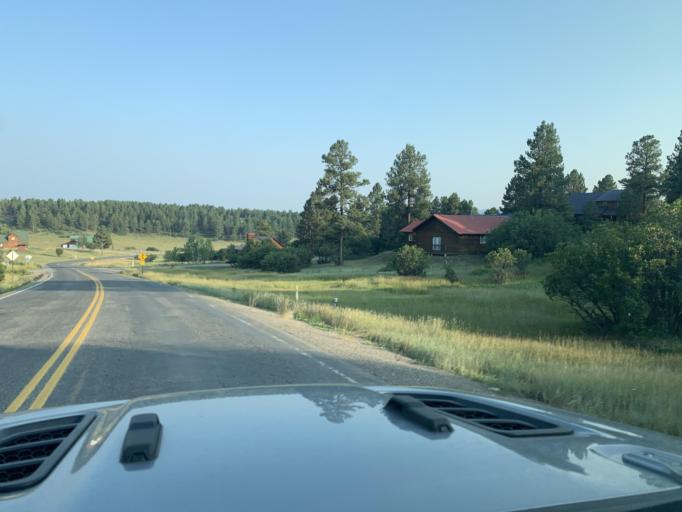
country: US
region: Colorado
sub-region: Archuleta County
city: Pagosa Springs
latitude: 37.2884
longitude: -107.0976
